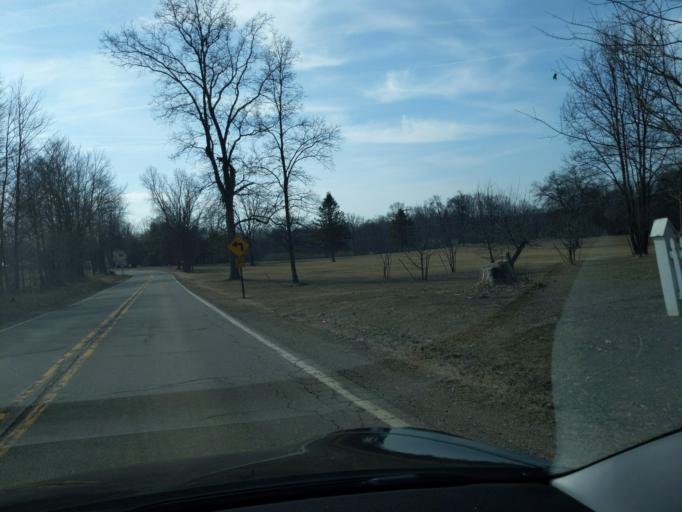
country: US
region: Michigan
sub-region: Ingham County
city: Stockbridge
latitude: 42.4499
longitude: -84.0763
